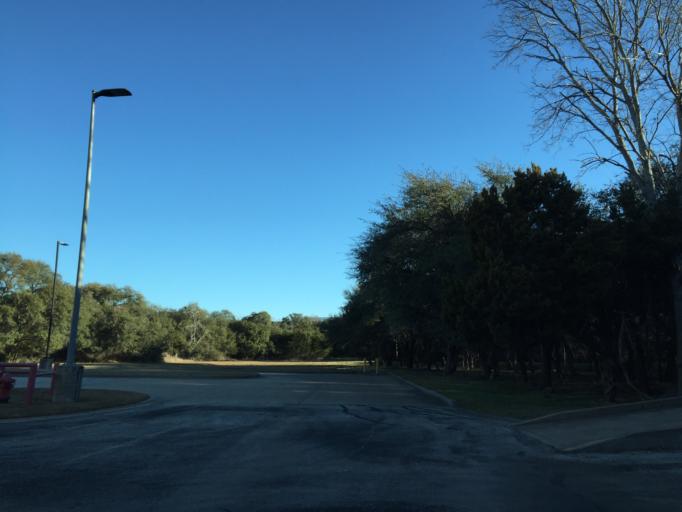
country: US
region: Texas
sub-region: Williamson County
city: Jollyville
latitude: 30.4233
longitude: -97.7440
